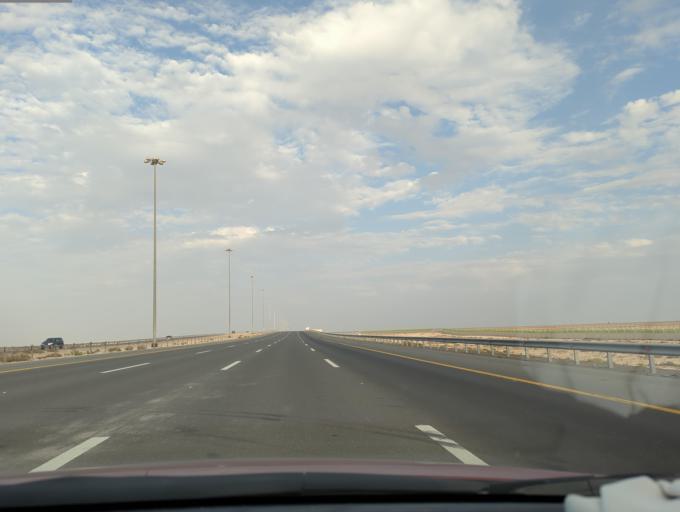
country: AE
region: Dubai
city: Dubai
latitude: 24.7445
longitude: 54.9002
